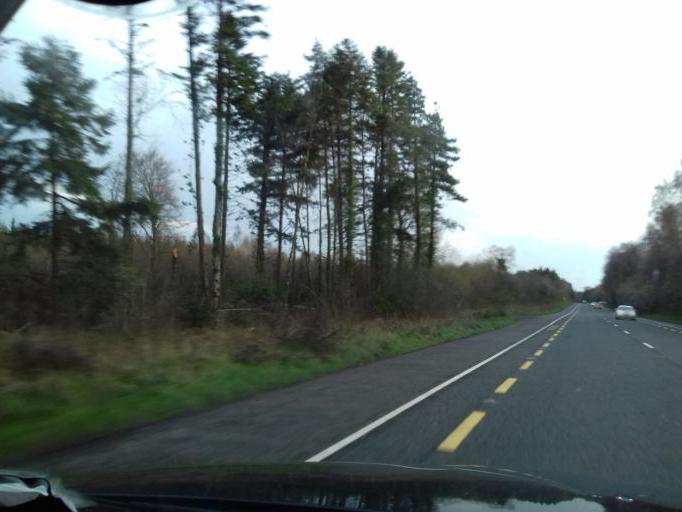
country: IE
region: Leinster
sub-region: Laois
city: Abbeyleix
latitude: 52.8952
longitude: -7.3609
